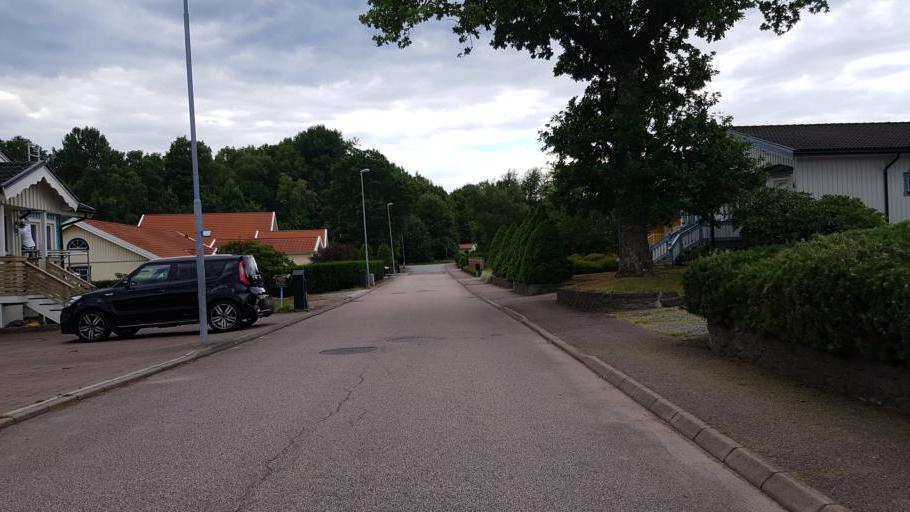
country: SE
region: Vaestra Goetaland
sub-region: Partille Kommun
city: Furulund
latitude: 57.7020
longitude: 12.1381
